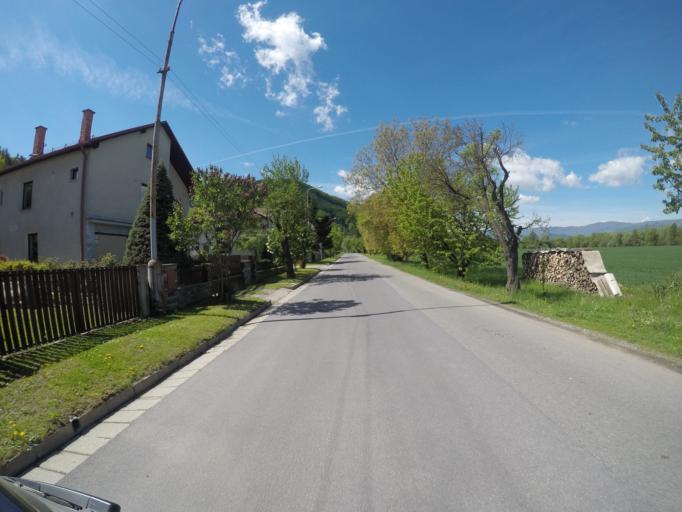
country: SK
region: Banskobystricky
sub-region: Okres Banska Bystrica
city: Banska Bystrica
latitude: 48.7359
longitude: 19.2043
